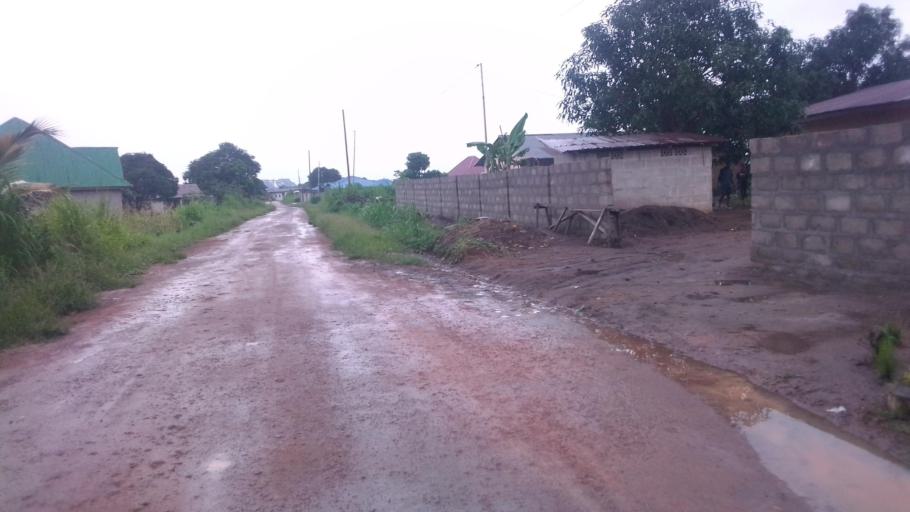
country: SL
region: Eastern Province
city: Hangha
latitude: 7.9116
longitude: -11.1643
